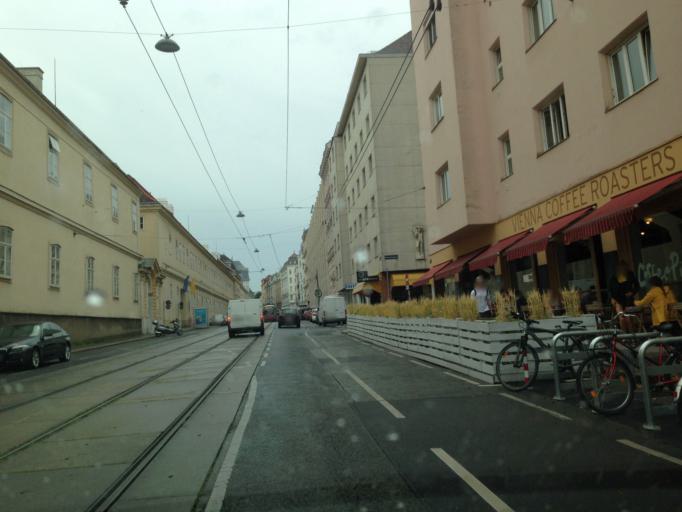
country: AT
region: Vienna
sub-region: Wien Stadt
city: Vienna
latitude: 48.2176
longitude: 16.3514
